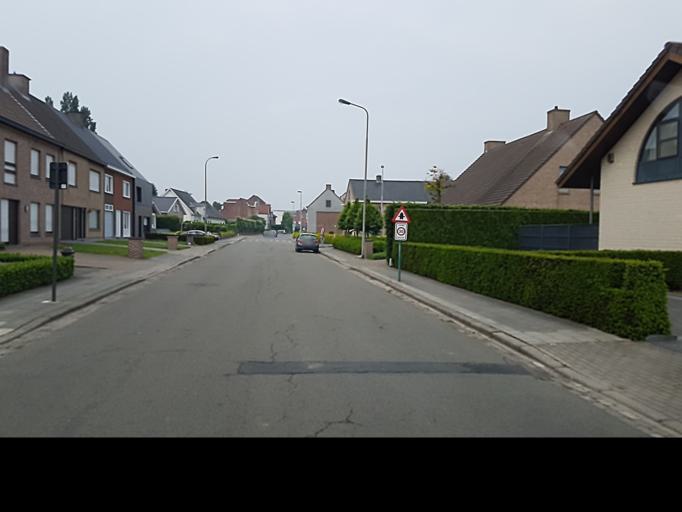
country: BE
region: Flanders
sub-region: Provincie West-Vlaanderen
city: Tielt
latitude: 51.0012
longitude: 3.3382
